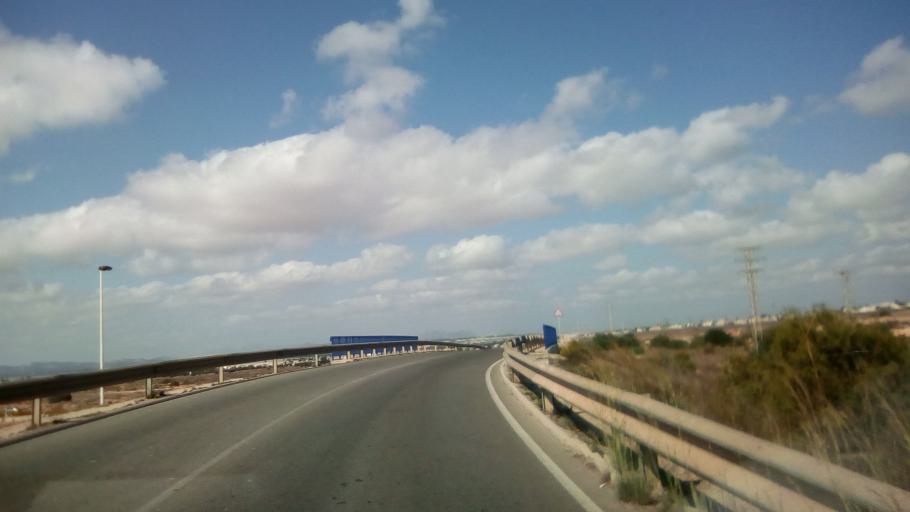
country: ES
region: Valencia
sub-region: Provincia de Alicante
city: Torrevieja
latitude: 37.9994
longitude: -0.6788
